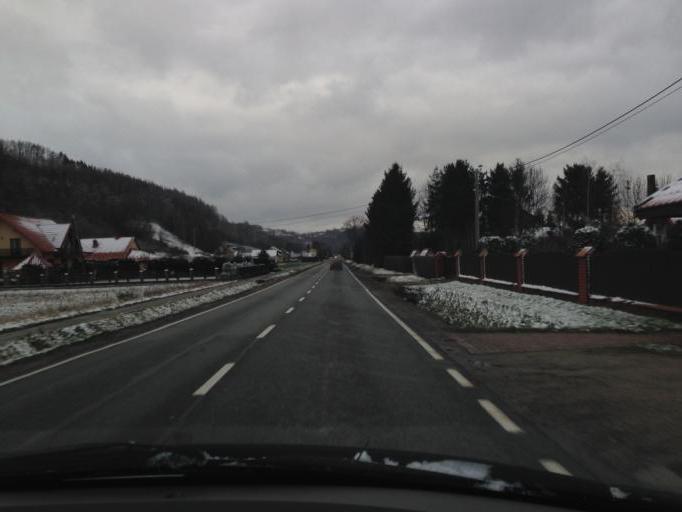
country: PL
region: Lesser Poland Voivodeship
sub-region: Powiat brzeski
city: Zlota
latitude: 49.8654
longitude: 20.7383
